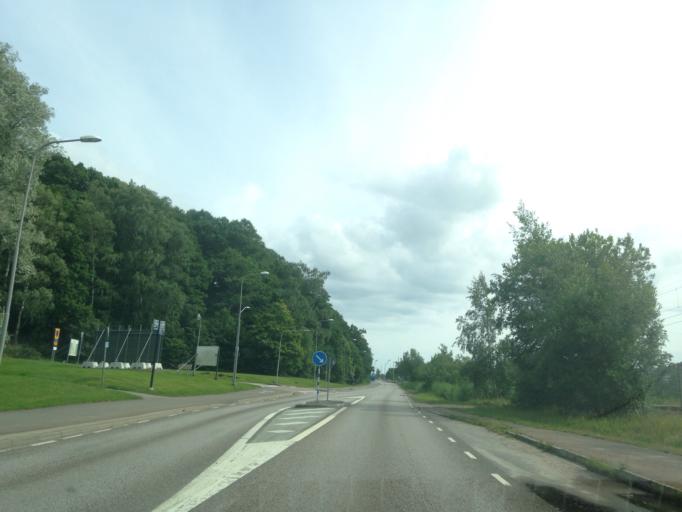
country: SE
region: Vaestra Goetaland
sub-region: Goteborg
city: Goeteborg
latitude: 57.7570
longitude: 11.9465
